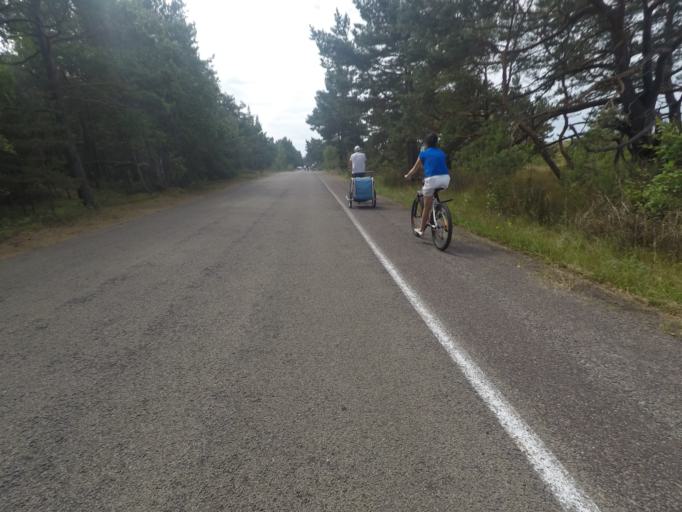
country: LT
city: Neringa
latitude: 55.5297
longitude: 21.0980
